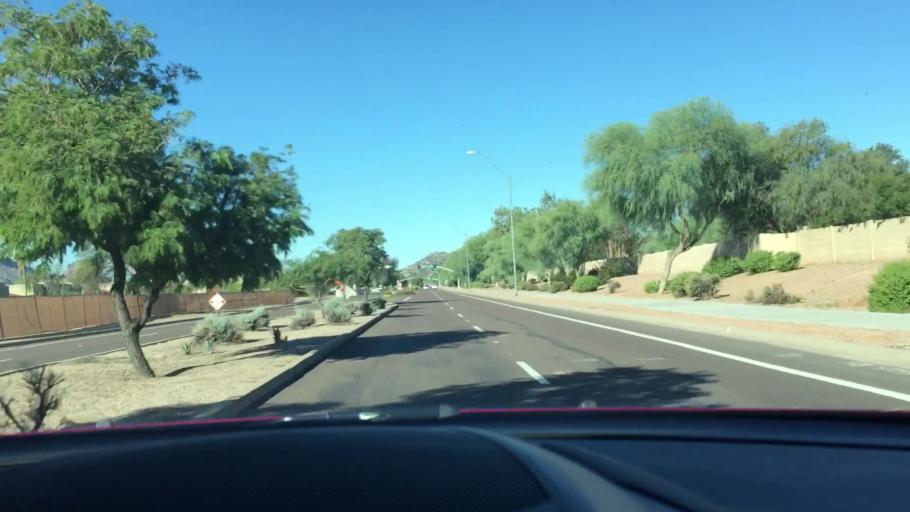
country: US
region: Arizona
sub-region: Maricopa County
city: Scottsdale
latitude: 33.5385
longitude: -111.9020
